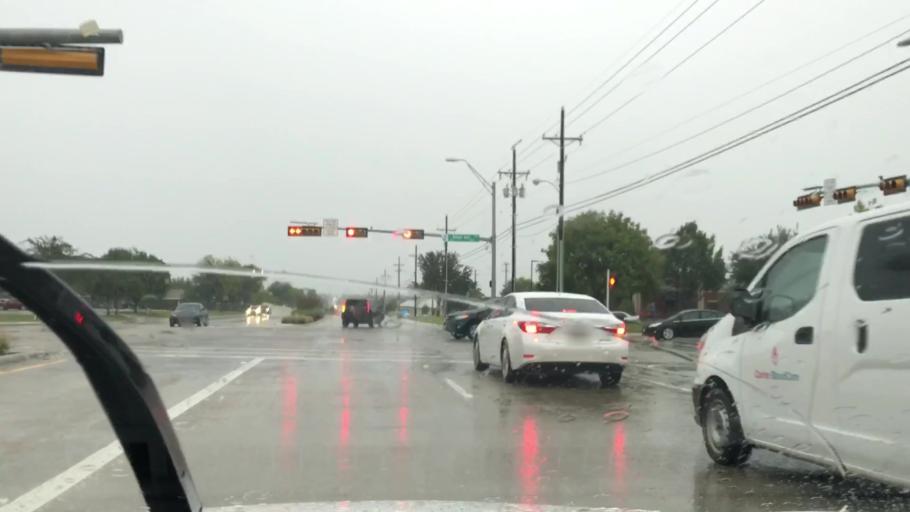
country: US
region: Texas
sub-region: Rockwall County
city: Rockwall
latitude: 32.8894
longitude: -96.4687
